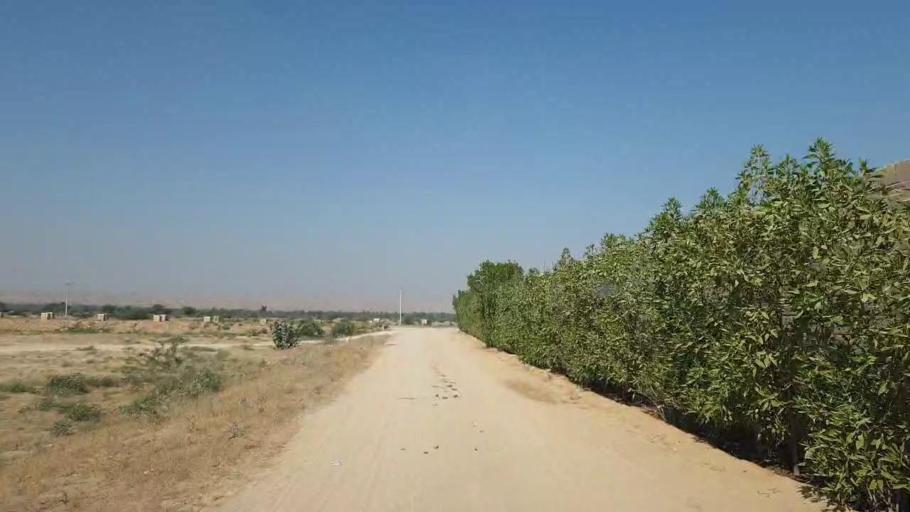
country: PK
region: Sindh
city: Jamshoro
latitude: 25.3693
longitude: 67.8408
